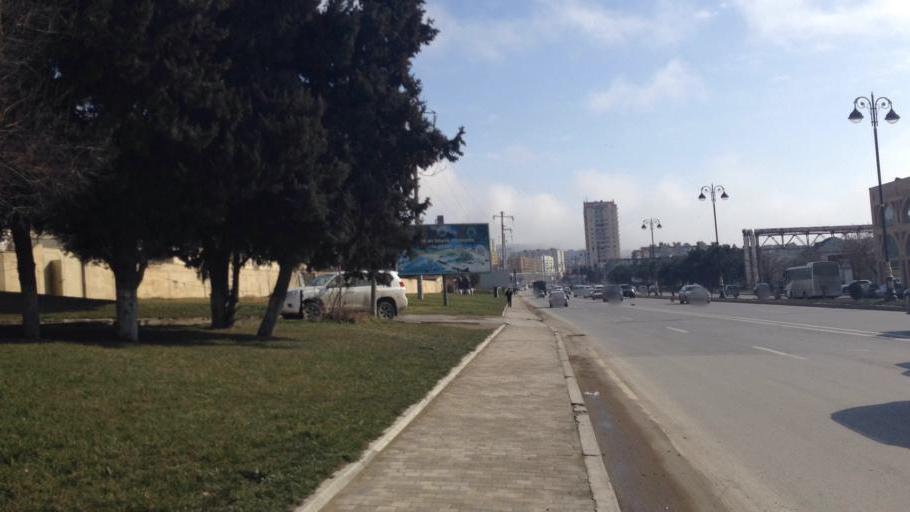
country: AZ
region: Baki
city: Baku
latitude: 40.3701
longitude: 49.9326
